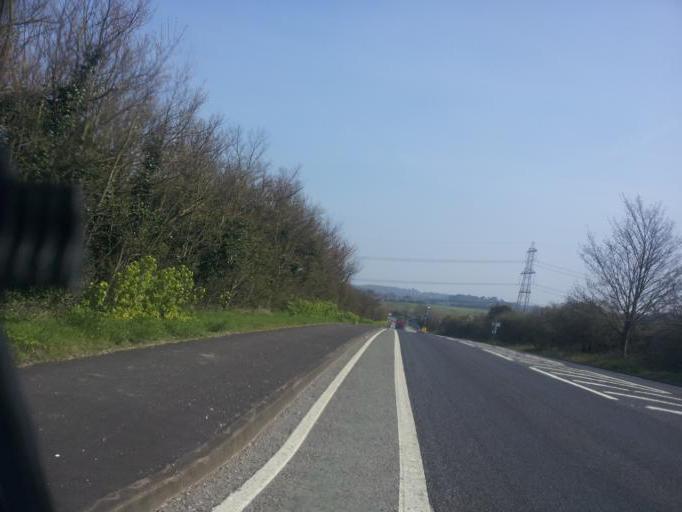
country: GB
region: England
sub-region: Kent
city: Gravesend
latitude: 51.4247
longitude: 0.4201
